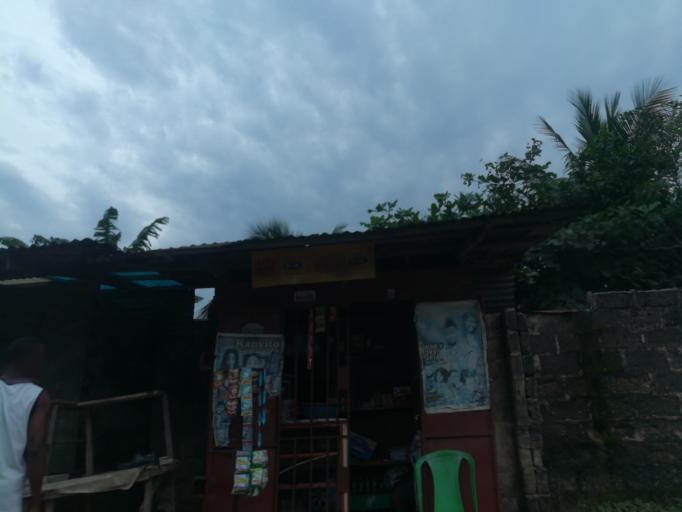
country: NG
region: Rivers
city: Port Harcourt
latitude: 4.8047
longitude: 6.9537
